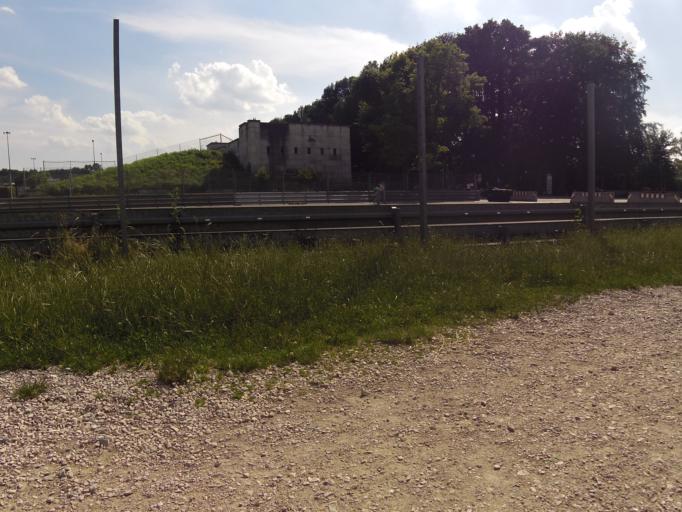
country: DE
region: Bavaria
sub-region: Regierungsbezirk Mittelfranken
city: Nuernberg
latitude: 49.4322
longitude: 11.1230
